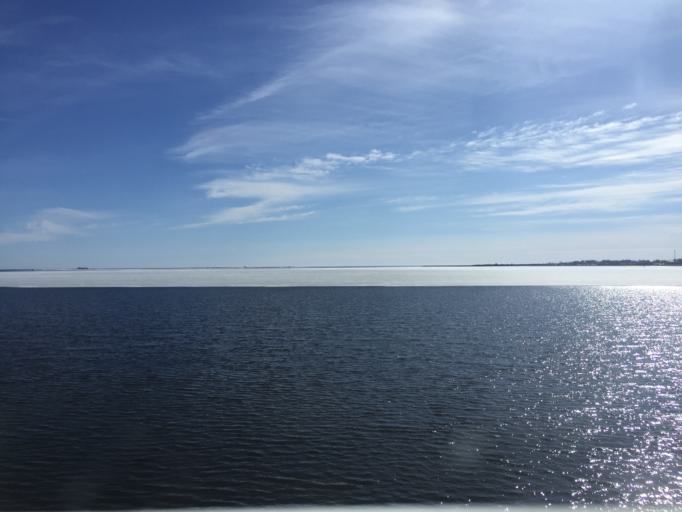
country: EE
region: Saare
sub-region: Orissaare vald
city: Orissaare
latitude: 58.5739
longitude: 23.4020
